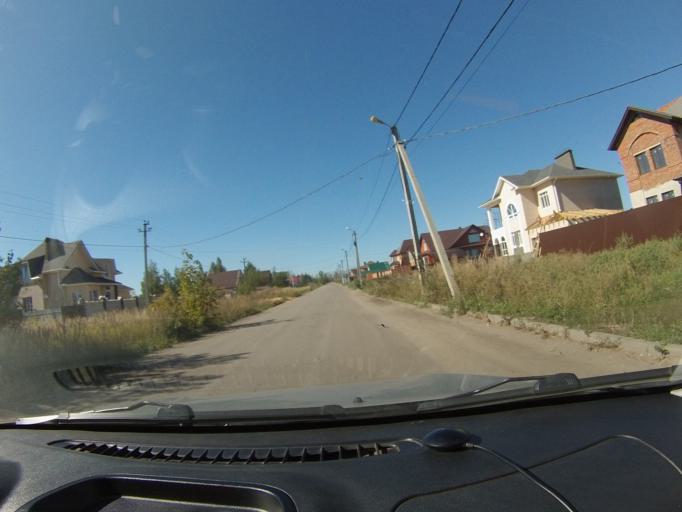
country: RU
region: Tambov
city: Tambov
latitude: 52.7672
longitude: 41.3762
